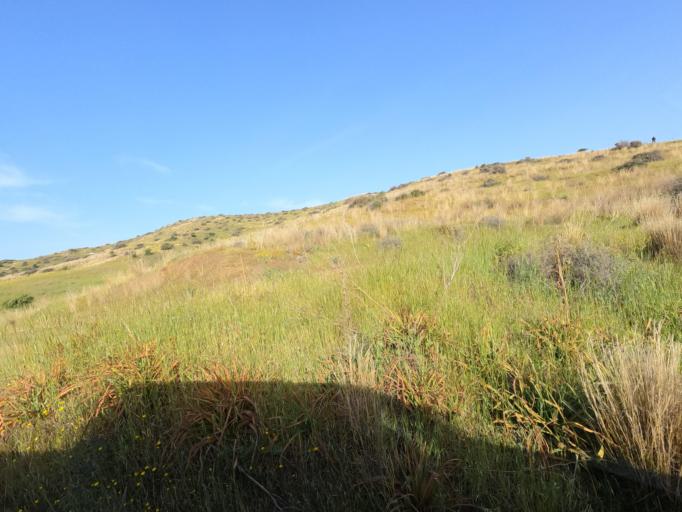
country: CY
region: Lefkosia
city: Lefka
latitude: 35.0823
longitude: 32.9354
